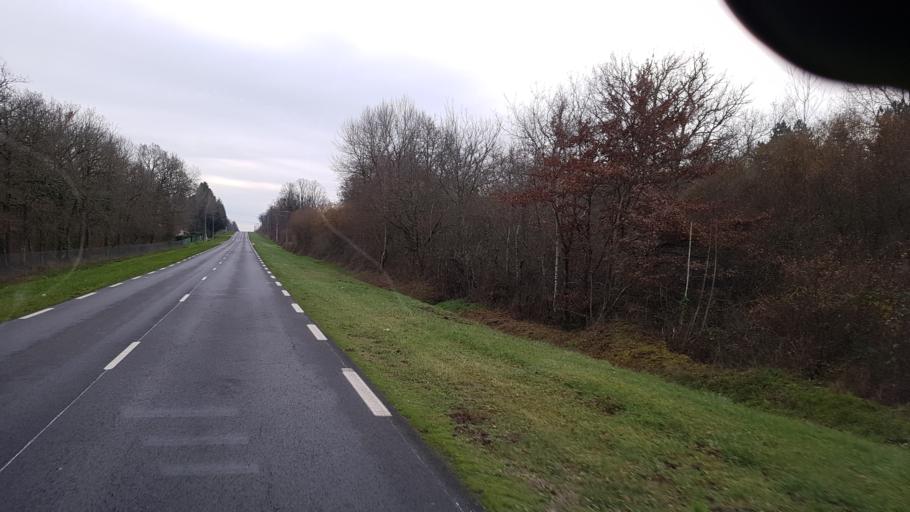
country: FR
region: Centre
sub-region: Departement du Loir-et-Cher
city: Nouan-le-Fuzelier
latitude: 47.5118
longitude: 2.0361
